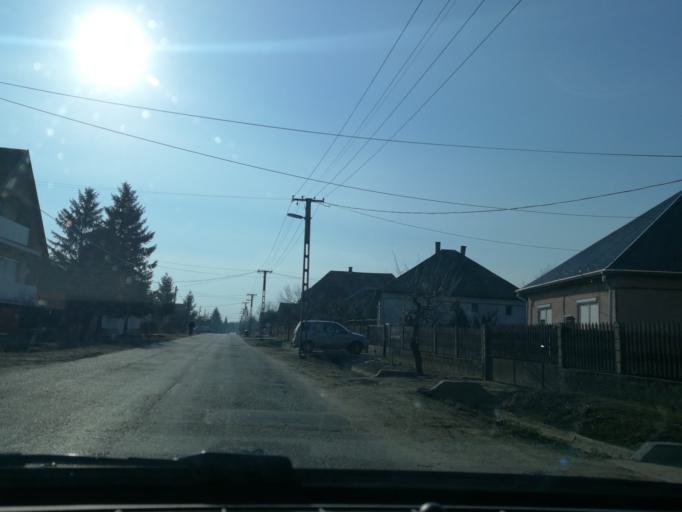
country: HU
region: Szabolcs-Szatmar-Bereg
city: Levelek
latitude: 47.9719
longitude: 21.9797
